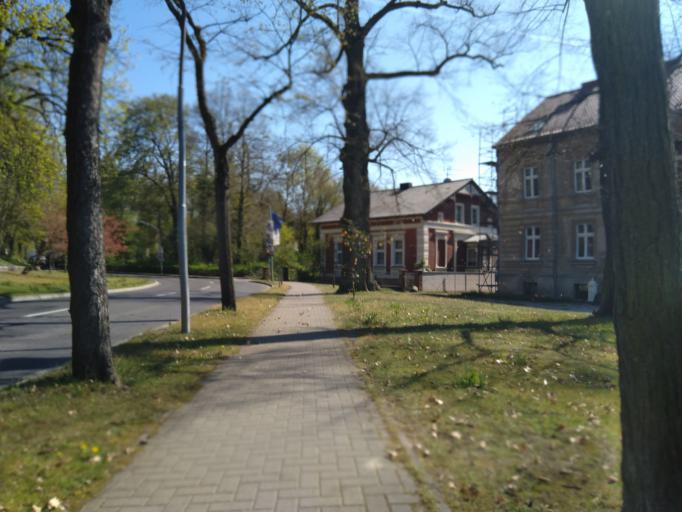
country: DE
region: Brandenburg
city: Biesenthal
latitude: 52.7640
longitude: 13.6456
